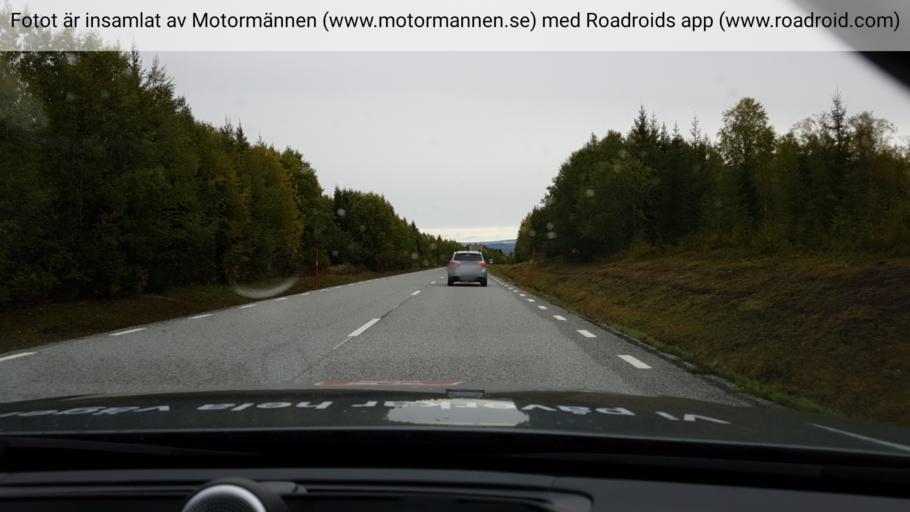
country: SE
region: Jaemtland
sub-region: Stroemsunds Kommun
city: Stroemsund
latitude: 64.1217
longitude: 15.6278
